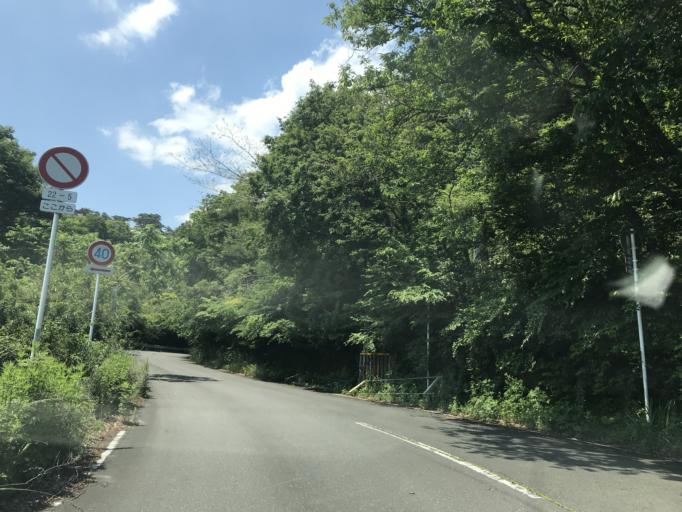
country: JP
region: Miyagi
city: Matsushima
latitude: 38.3533
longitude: 141.0585
